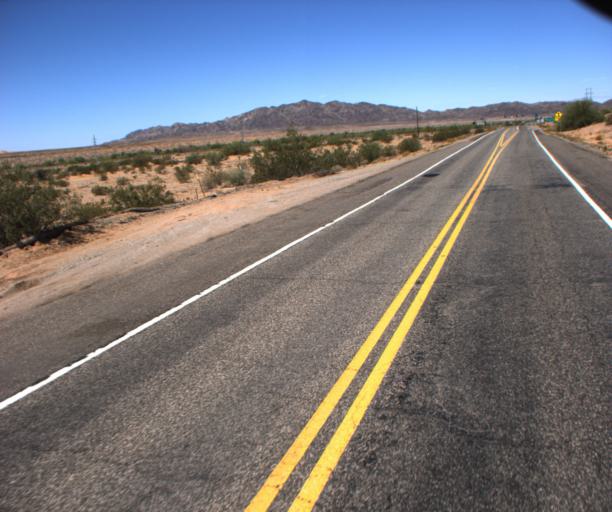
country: US
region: Arizona
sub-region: La Paz County
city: Parker
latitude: 33.9939
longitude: -114.2129
